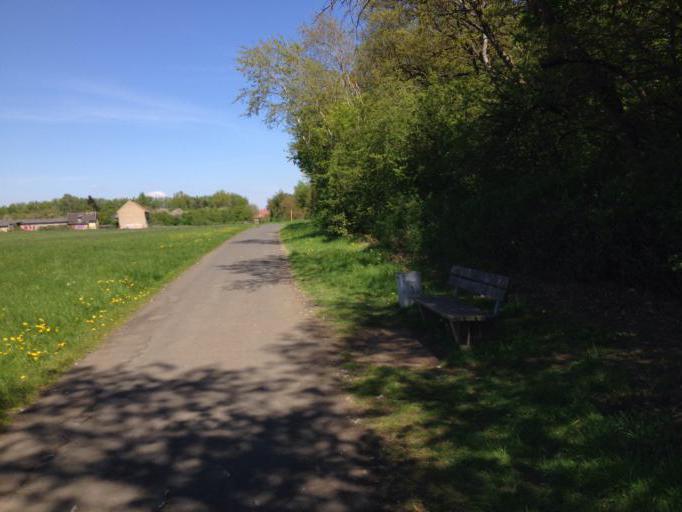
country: DE
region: Hesse
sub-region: Regierungsbezirk Giessen
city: Giessen
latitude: 50.5626
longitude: 8.6639
